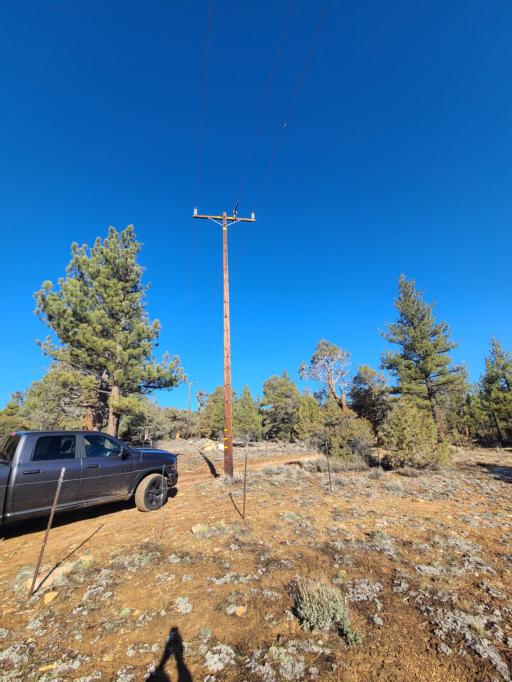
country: US
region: California
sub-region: San Bernardino County
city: Big Bear City
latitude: 34.3057
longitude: -116.8479
